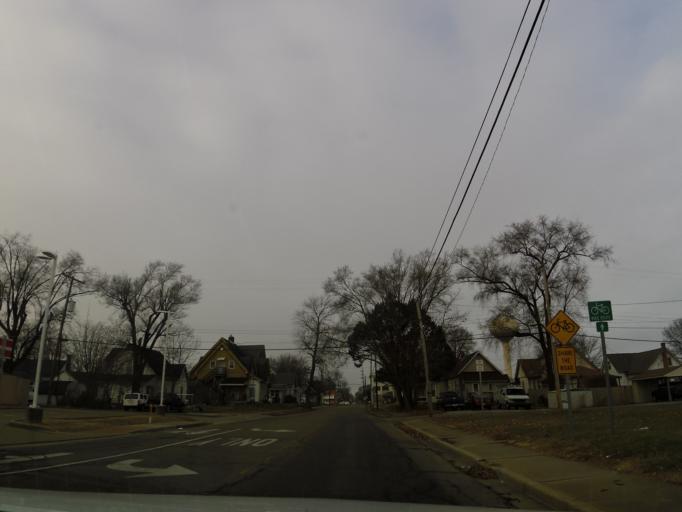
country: US
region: Indiana
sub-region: Bartholomew County
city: Columbus
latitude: 39.2159
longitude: -85.9043
